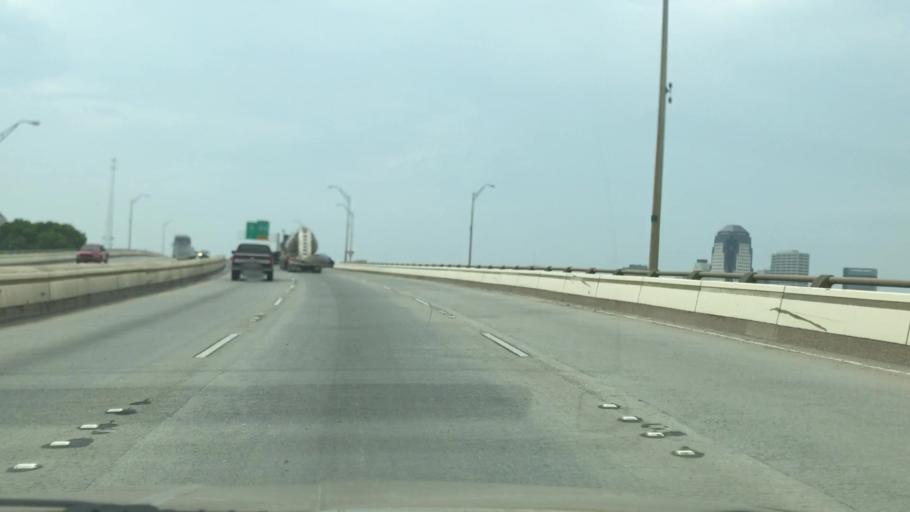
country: US
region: Louisiana
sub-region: Bossier Parish
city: Bossier City
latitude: 32.5128
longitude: -93.7366
